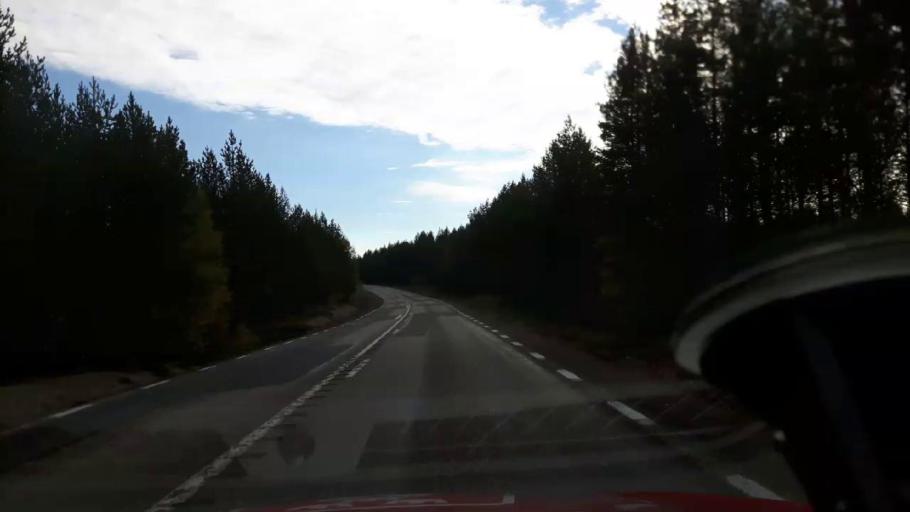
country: SE
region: Gaevleborg
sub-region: Ljusdals Kommun
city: Farila
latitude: 61.9384
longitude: 15.3906
